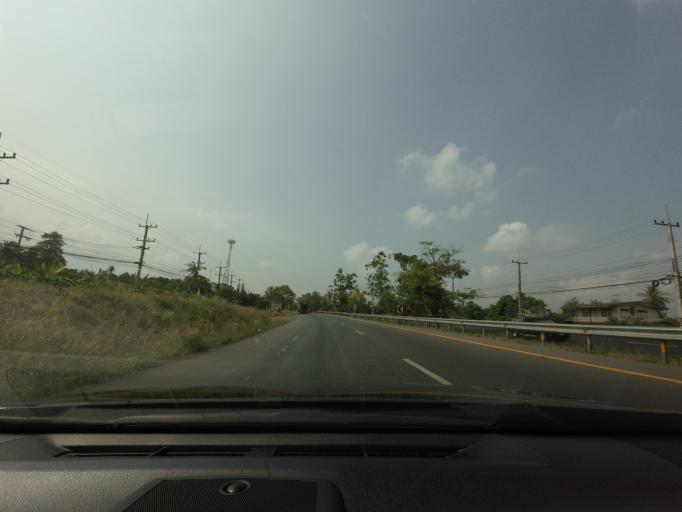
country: TH
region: Prachuap Khiri Khan
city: Sam Roi Yot
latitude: 12.2607
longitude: 99.8692
